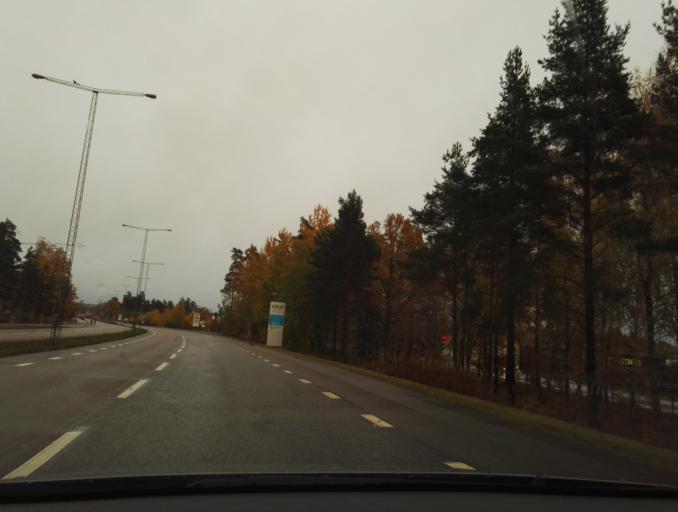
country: SE
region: Kronoberg
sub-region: Vaxjo Kommun
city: Vaexjoe
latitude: 56.8792
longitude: 14.7670
